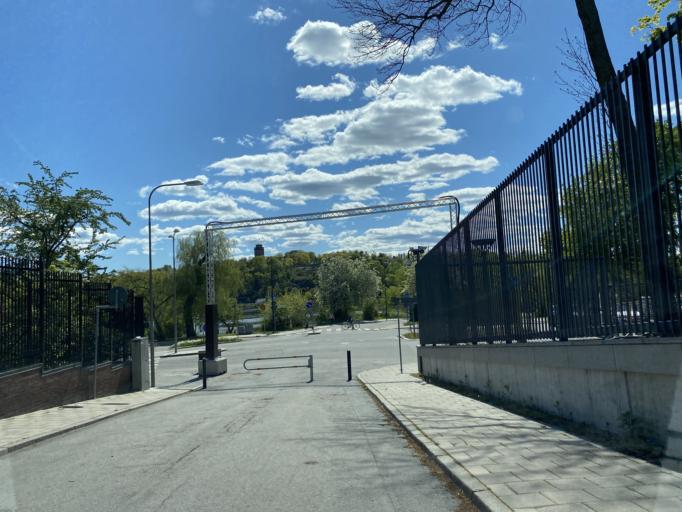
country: SE
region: Stockholm
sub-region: Stockholms Kommun
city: OEstermalm
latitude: 59.3335
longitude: 18.1071
